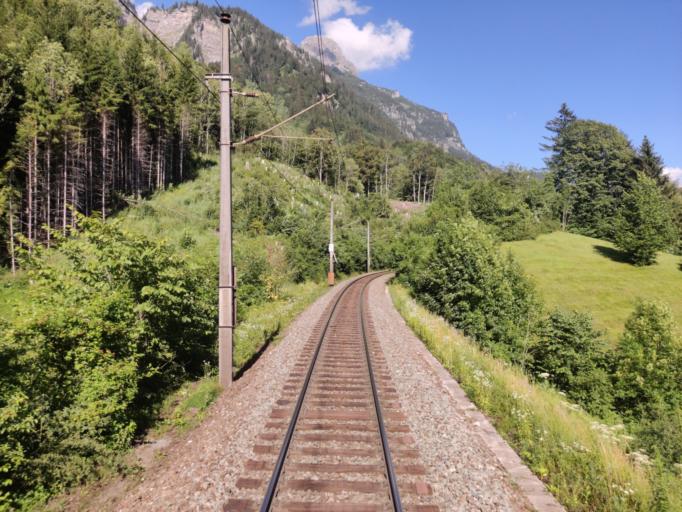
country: AT
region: Vorarlberg
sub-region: Politischer Bezirk Bludenz
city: Innerbraz
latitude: 47.1488
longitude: 9.9140
